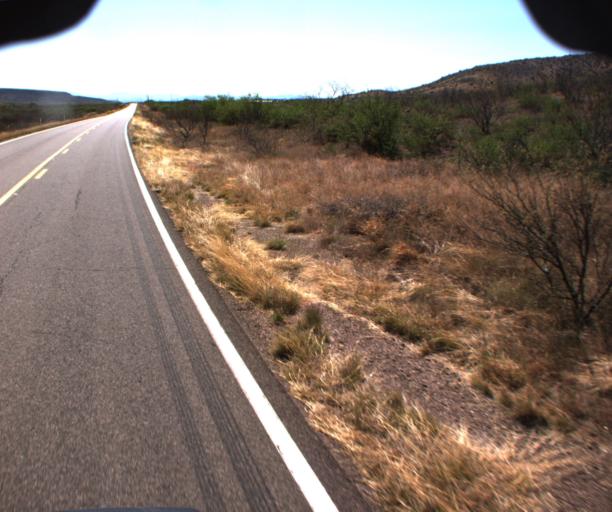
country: US
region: Arizona
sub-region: Cochise County
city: Douglas
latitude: 31.4902
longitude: -109.4231
